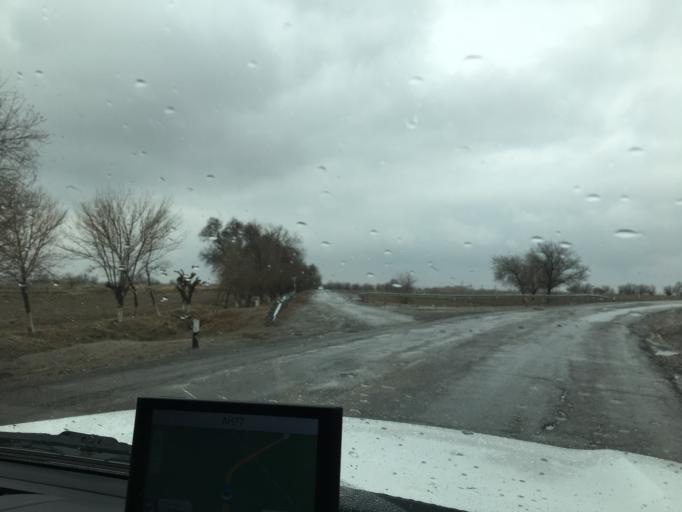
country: TM
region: Mary
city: Yoloeten
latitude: 37.3873
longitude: 62.1819
